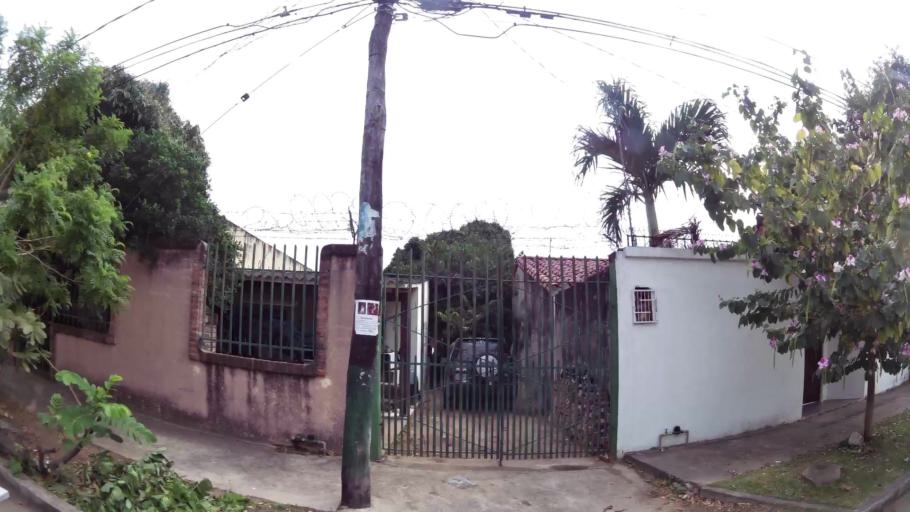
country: BO
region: Santa Cruz
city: Santa Cruz de la Sierra
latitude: -17.7733
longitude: -63.2060
